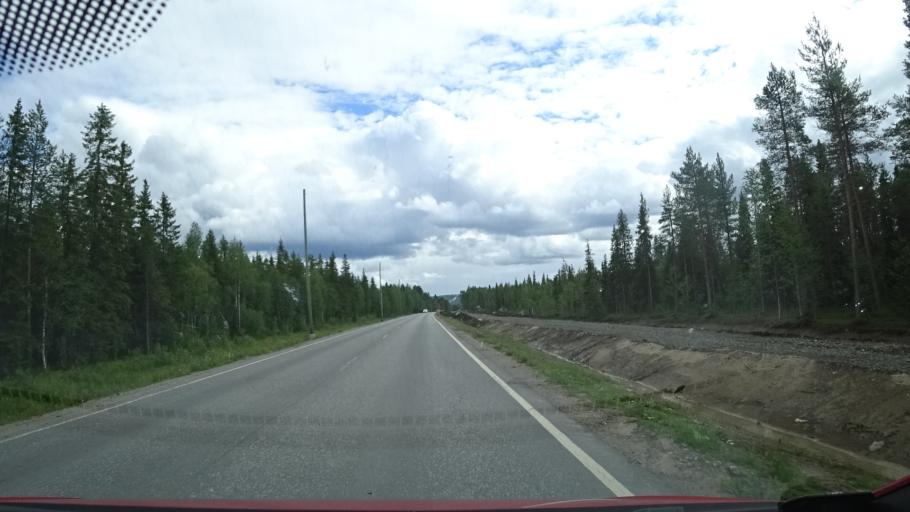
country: FI
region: Lapland
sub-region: Rovaniemi
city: Rovaniemi
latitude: 66.5361
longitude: 25.7275
